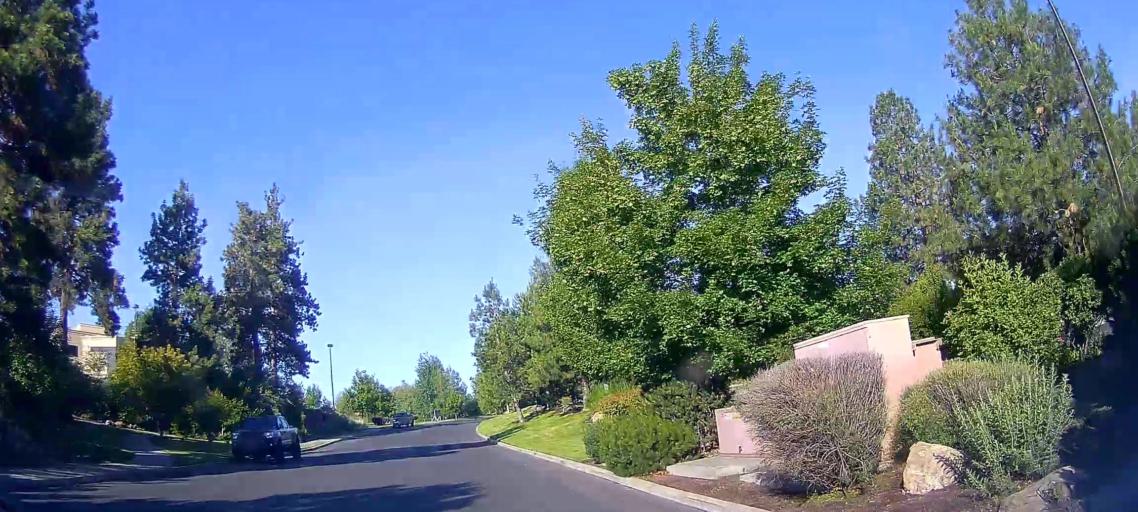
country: US
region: Oregon
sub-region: Deschutes County
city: Bend
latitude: 44.0439
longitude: -121.3228
